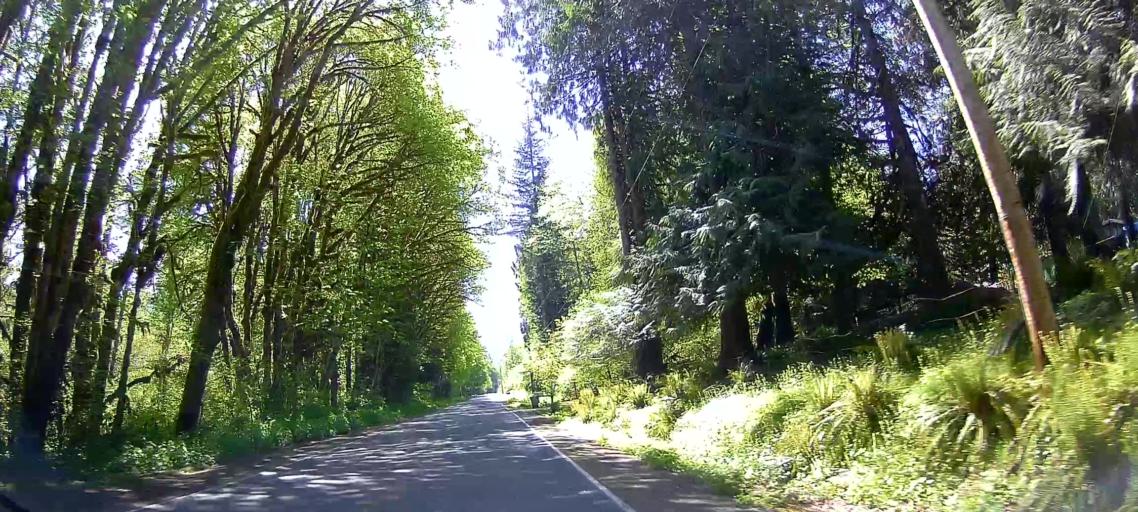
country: US
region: Washington
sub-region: Snohomish County
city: Darrington
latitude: 48.4941
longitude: -121.6583
